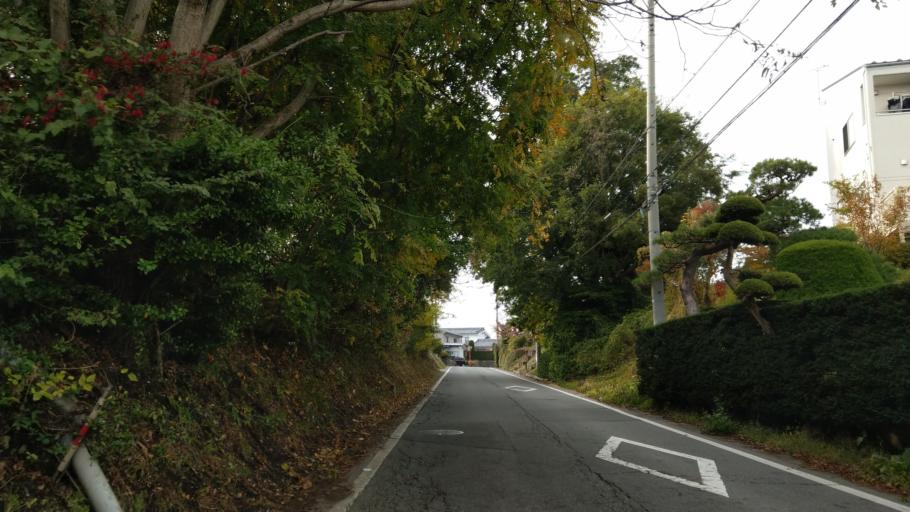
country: JP
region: Nagano
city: Komoro
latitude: 36.3137
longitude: 138.4408
